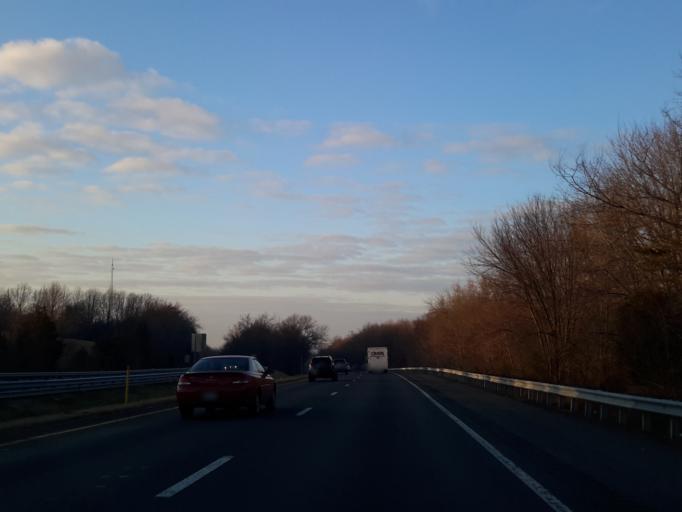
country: US
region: Maryland
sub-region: Montgomery County
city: Clarksburg
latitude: 39.2526
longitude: -77.3019
